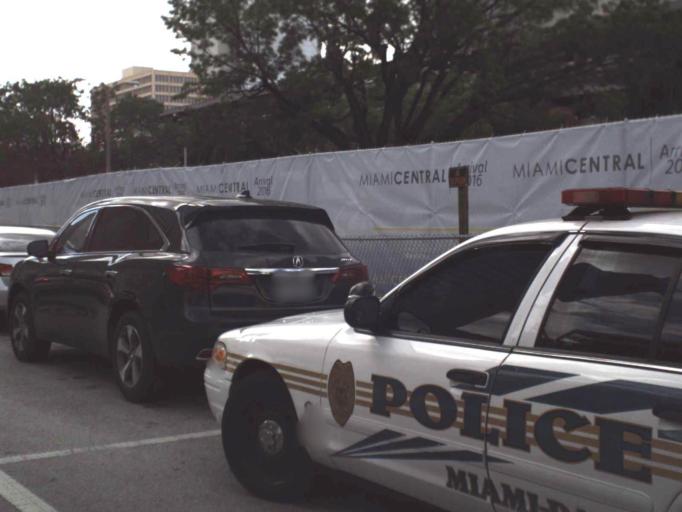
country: US
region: Florida
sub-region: Miami-Dade County
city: Miami
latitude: 25.7768
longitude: -80.1953
